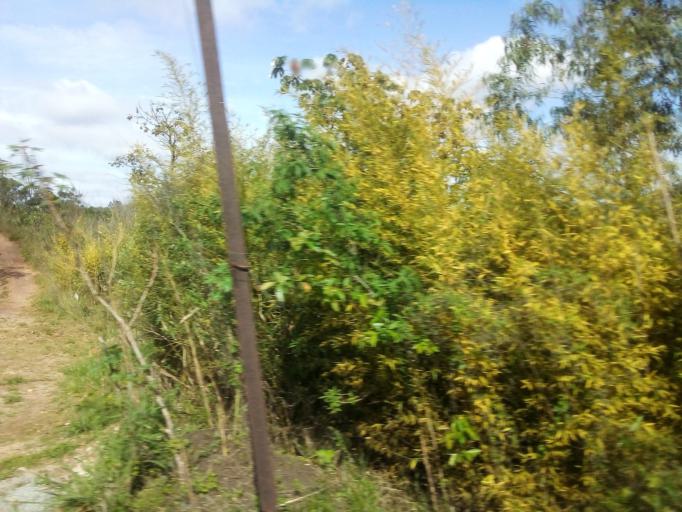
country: BR
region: Minas Gerais
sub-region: Raposos
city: Raposos
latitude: -19.8832
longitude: -43.7659
